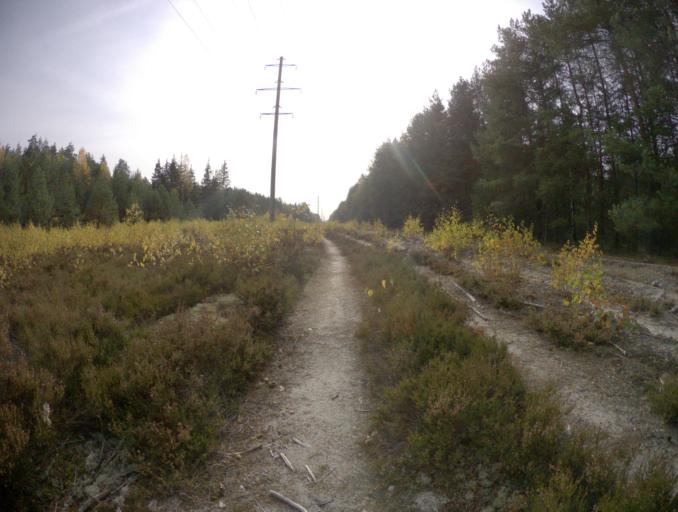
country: RU
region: Vladimir
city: Vorsha
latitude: 55.9658
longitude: 40.1459
